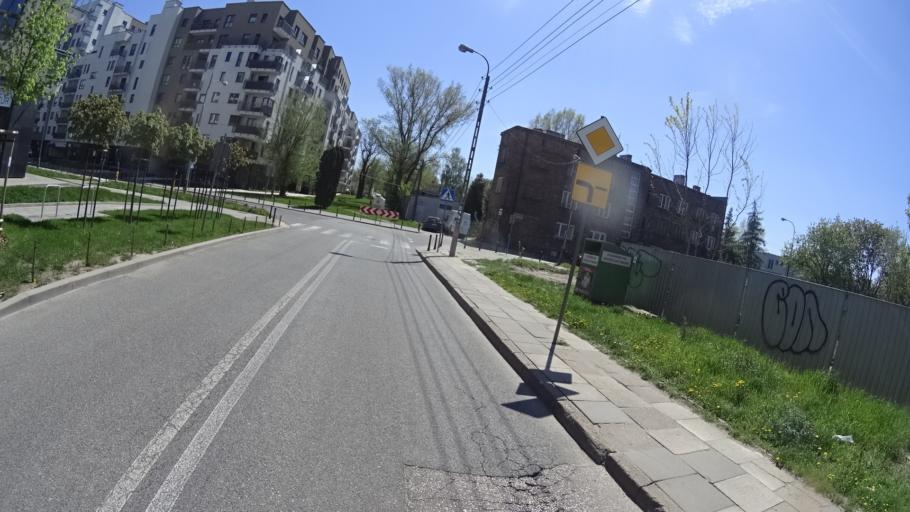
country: PL
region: Masovian Voivodeship
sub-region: Warszawa
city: Bemowo
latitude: 52.2217
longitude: 20.9291
